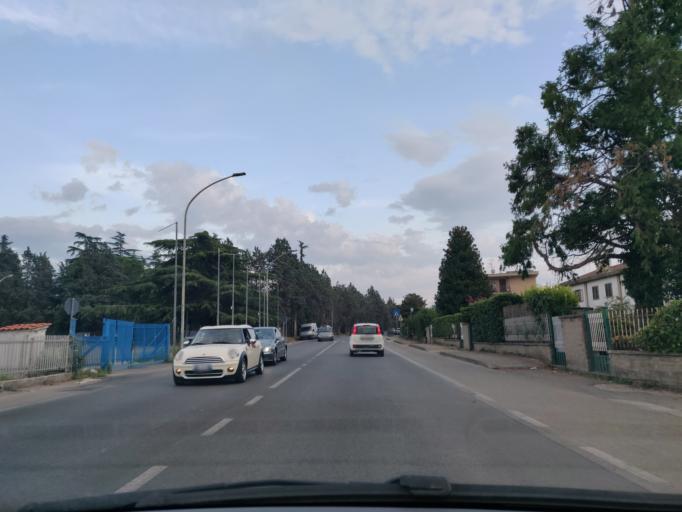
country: IT
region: Latium
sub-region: Provincia di Viterbo
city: Viterbo
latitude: 42.4362
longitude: 12.0968
